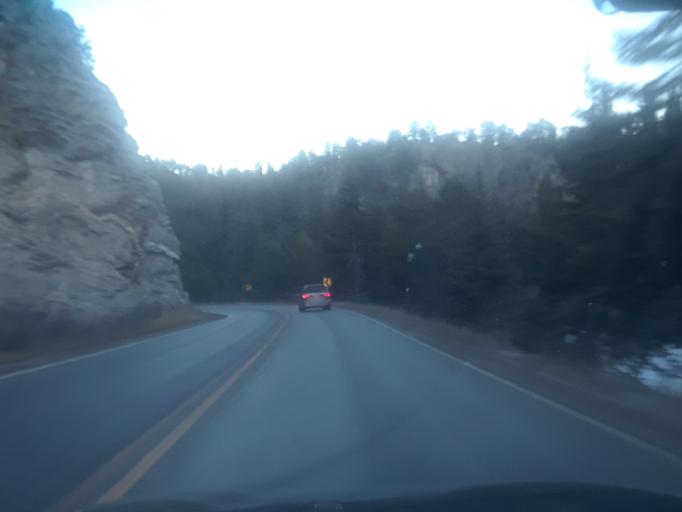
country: US
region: Colorado
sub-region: Jefferson County
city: Evergreen
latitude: 39.4102
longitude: -105.4983
